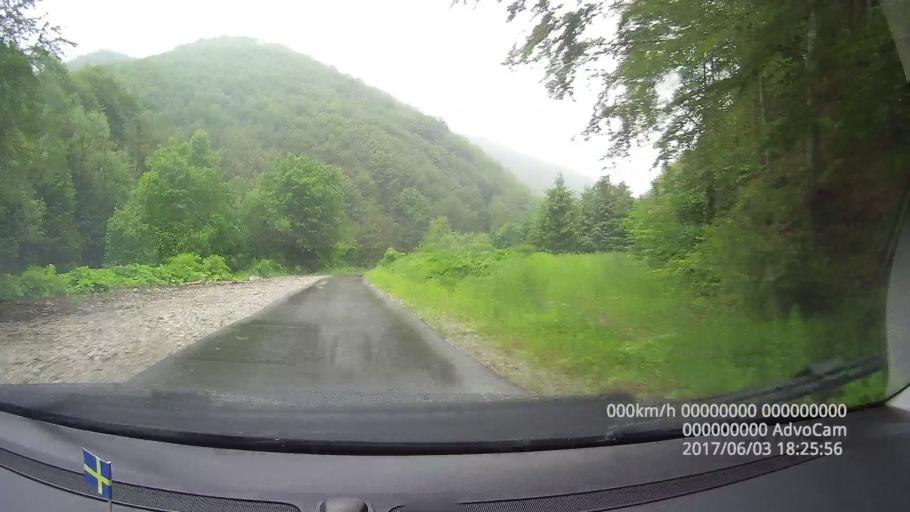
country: RO
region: Gorj
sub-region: Comuna Runcu
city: Dobrita
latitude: 45.1721
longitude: 23.1908
